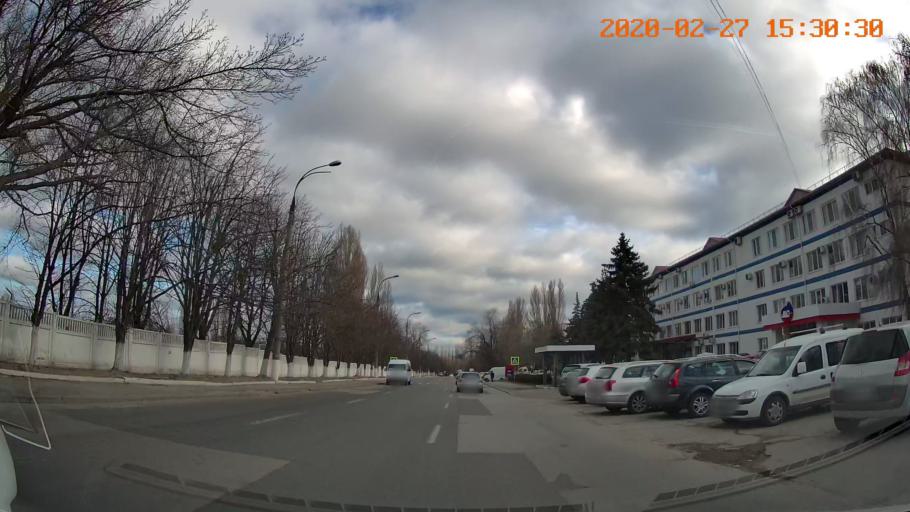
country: MD
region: Chisinau
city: Chisinau
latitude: 46.9819
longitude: 28.8800
